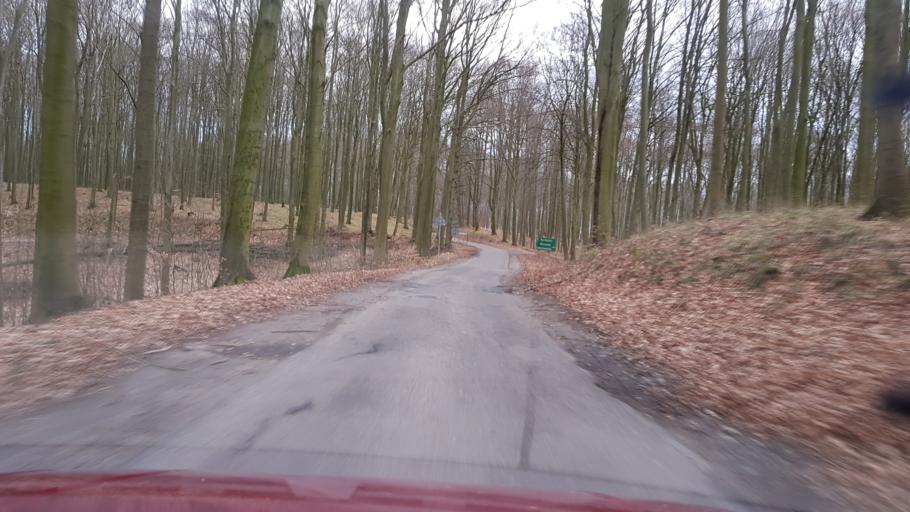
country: PL
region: West Pomeranian Voivodeship
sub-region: Szczecin
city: Szczecin
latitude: 53.3358
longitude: 14.6444
